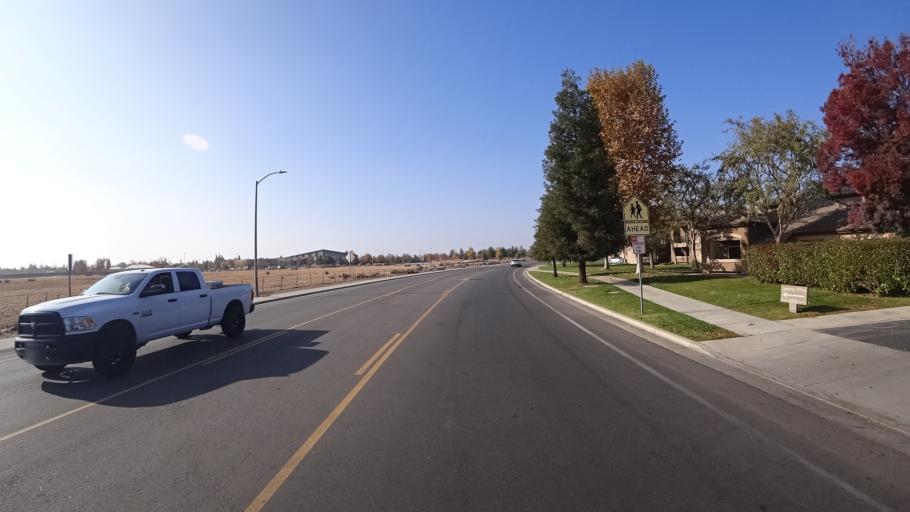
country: US
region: California
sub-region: Kern County
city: Greenacres
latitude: 35.3944
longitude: -119.0942
